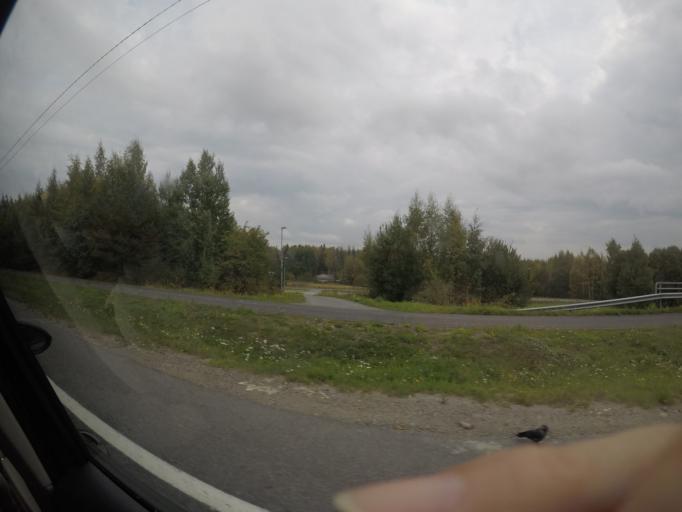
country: FI
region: Haeme
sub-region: Haemeenlinna
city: Haemeenlinna
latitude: 61.0235
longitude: 24.4223
